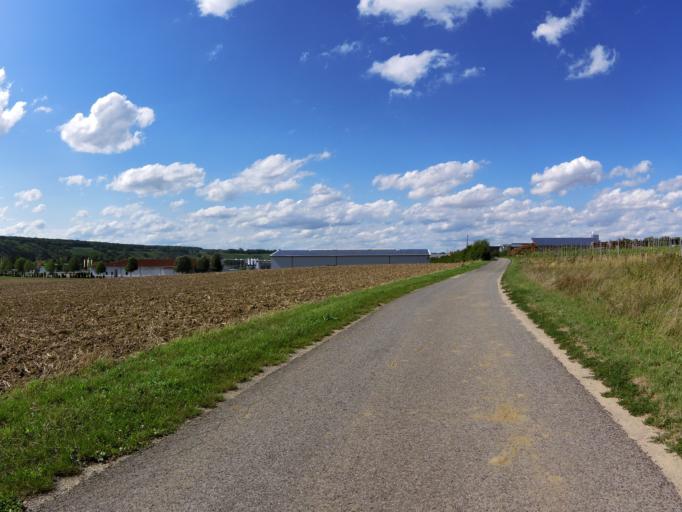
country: DE
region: Bavaria
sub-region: Regierungsbezirk Unterfranken
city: Segnitz
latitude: 49.6856
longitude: 10.1486
